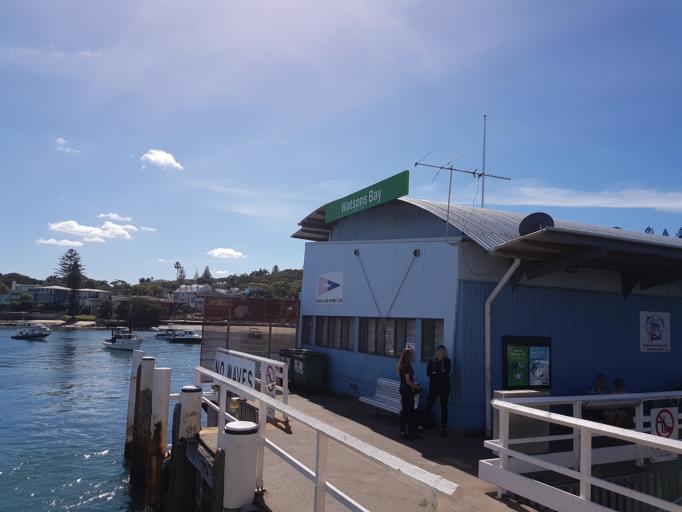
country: AU
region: New South Wales
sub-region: Waverley
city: Dover Heights
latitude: -33.8436
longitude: 151.2808
